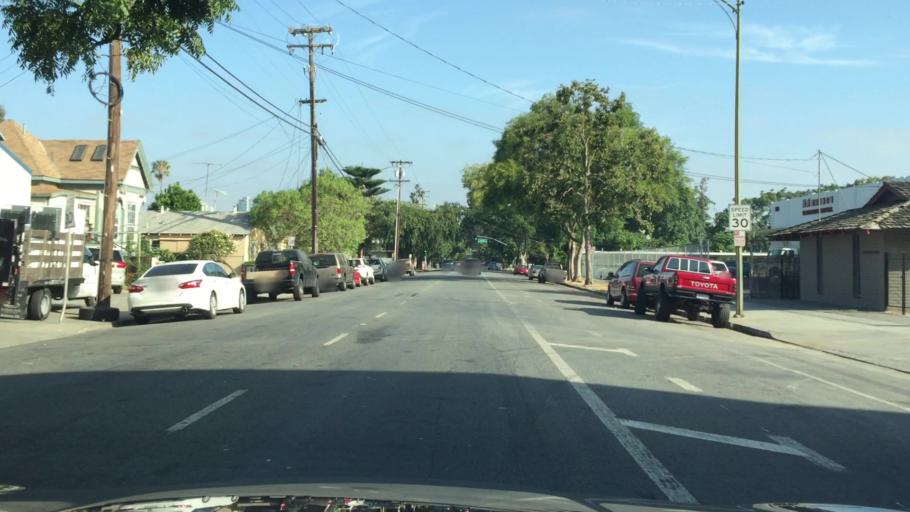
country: US
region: California
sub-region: Santa Clara County
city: San Jose
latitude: 37.3223
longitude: -121.8773
